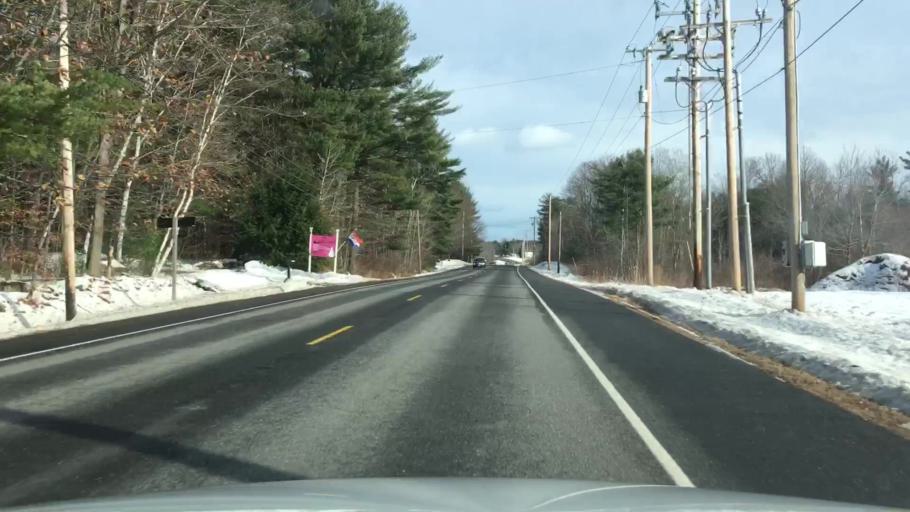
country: US
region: Maine
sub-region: Androscoggin County
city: Greene
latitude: 44.2007
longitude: -70.1152
